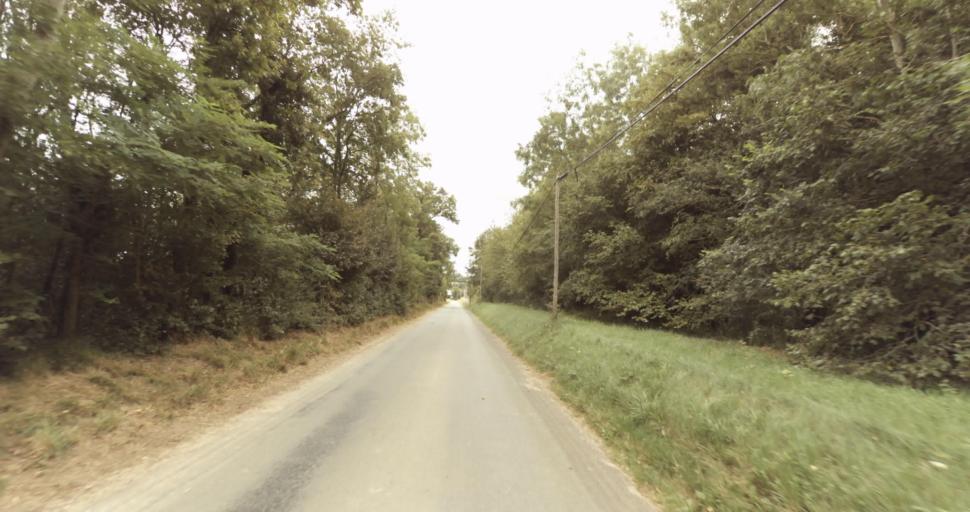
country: FR
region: Haute-Normandie
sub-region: Departement de l'Eure
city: Menilles
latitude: 49.0166
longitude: 1.3007
